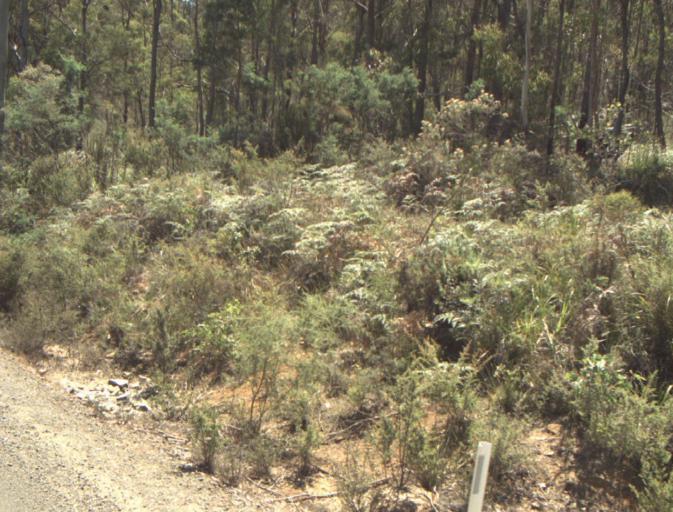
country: AU
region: Tasmania
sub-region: Launceston
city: Mayfield
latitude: -41.2754
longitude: 147.1079
